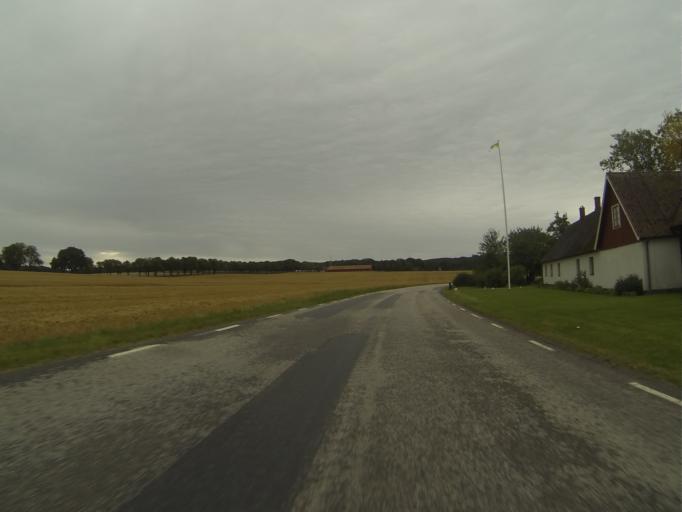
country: SE
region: Skane
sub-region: Lunds Kommun
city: Genarp
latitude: 55.6241
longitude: 13.3928
